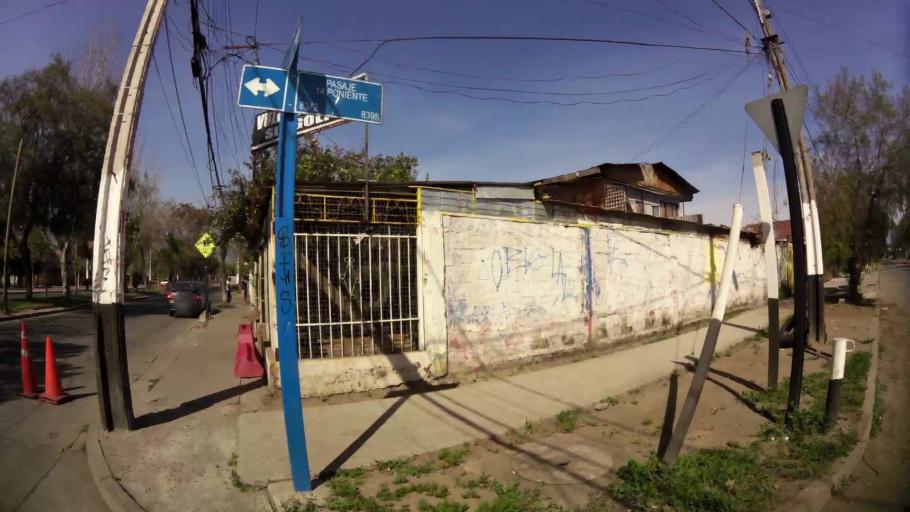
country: CL
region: Santiago Metropolitan
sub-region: Provincia de Santiago
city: La Pintana
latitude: -33.5375
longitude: -70.6327
